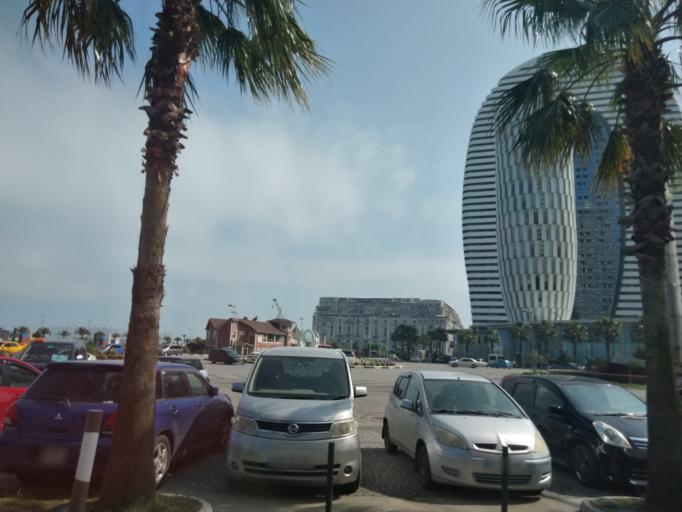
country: GE
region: Ajaria
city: Batumi
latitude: 41.6403
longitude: 41.6139
